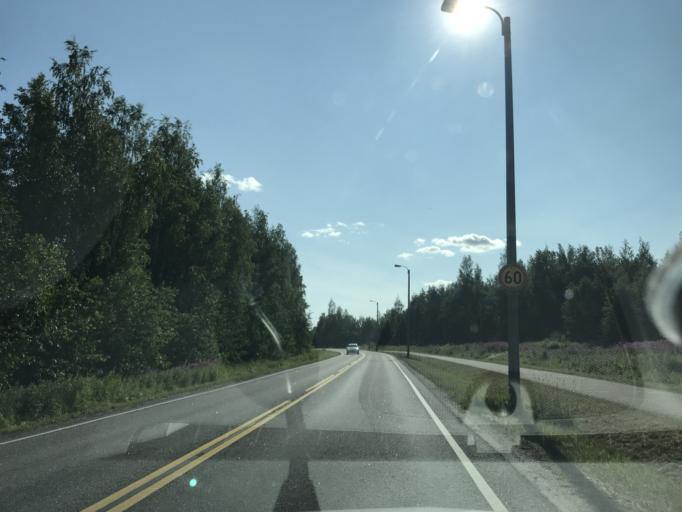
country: FI
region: Uusimaa
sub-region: Helsinki
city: Nurmijaervi
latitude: 60.3851
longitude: 24.7058
